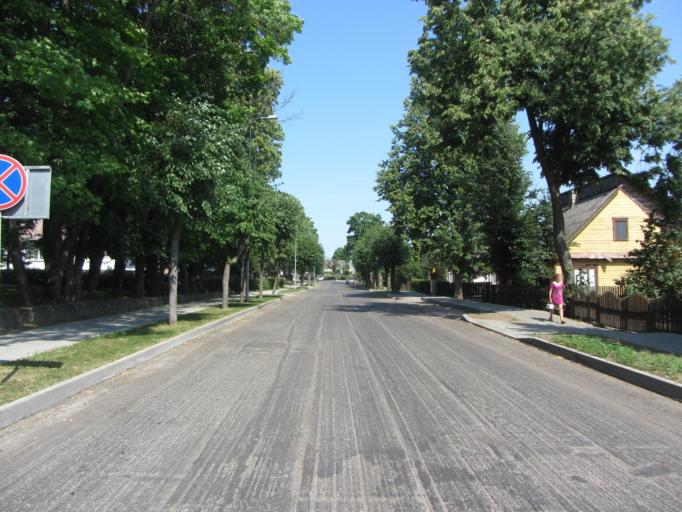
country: LT
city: Zarasai
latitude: 55.7332
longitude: 26.2539
